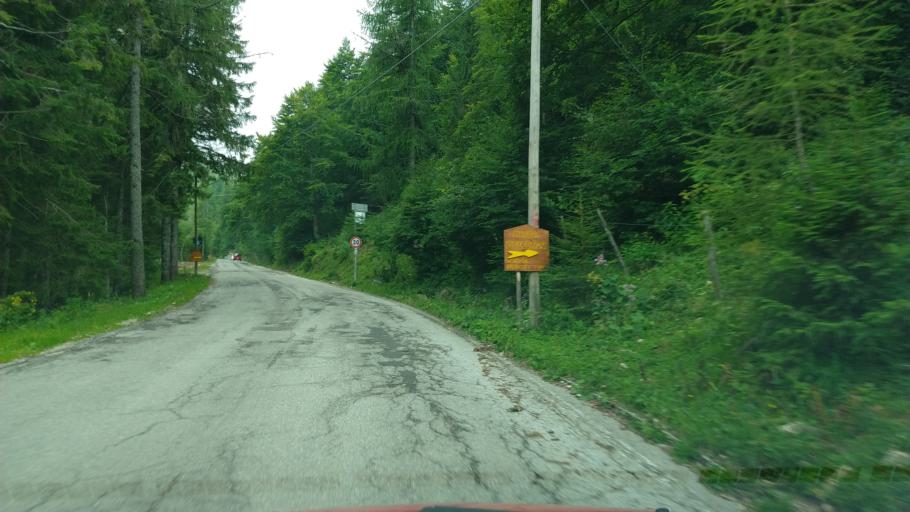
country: IT
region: Veneto
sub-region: Provincia di Vicenza
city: Pedemonte
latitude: 45.8801
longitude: 11.2970
